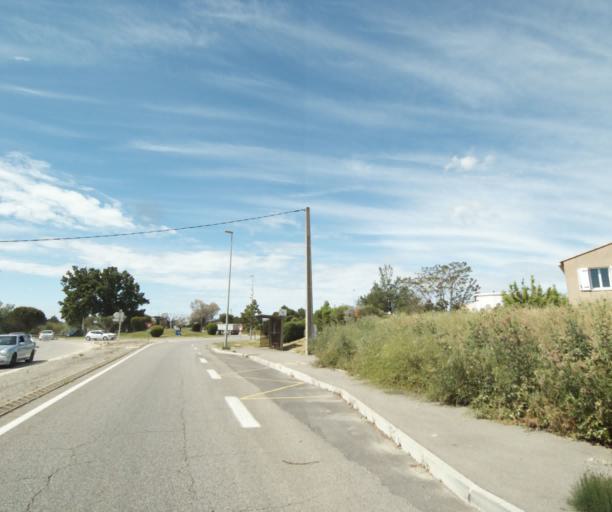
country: FR
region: Provence-Alpes-Cote d'Azur
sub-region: Departement des Bouches-du-Rhone
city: Rognac
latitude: 43.5049
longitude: 5.2215
